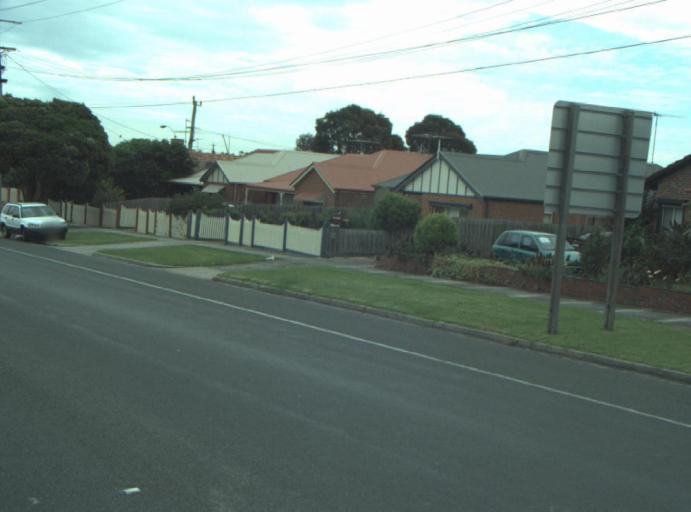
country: AU
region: Victoria
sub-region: Greater Geelong
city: East Geelong
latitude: -38.1699
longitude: 144.3843
